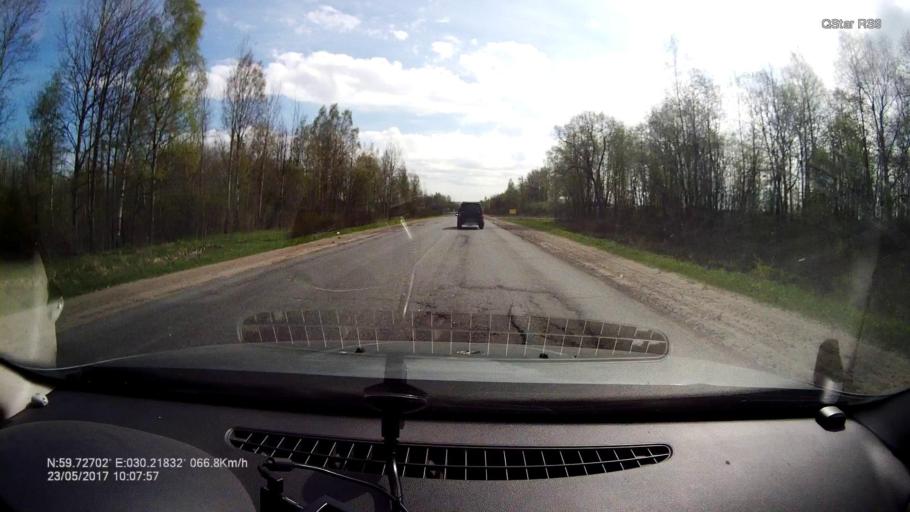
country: RU
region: St.-Petersburg
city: Gorelovo
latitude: 59.7270
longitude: 30.2185
